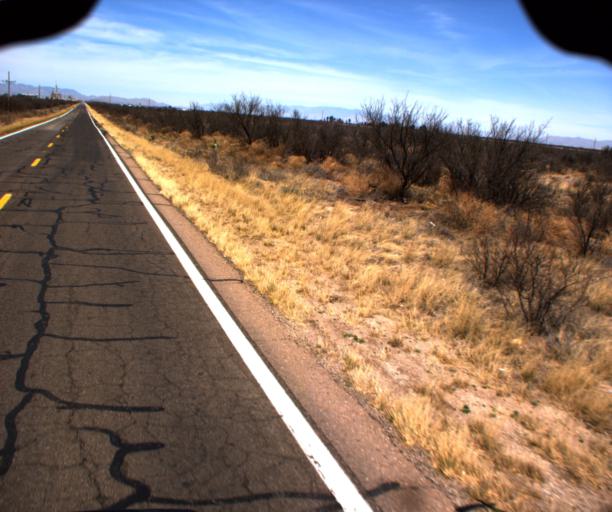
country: US
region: Arizona
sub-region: Cochise County
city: Willcox
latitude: 32.0147
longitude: -109.8683
